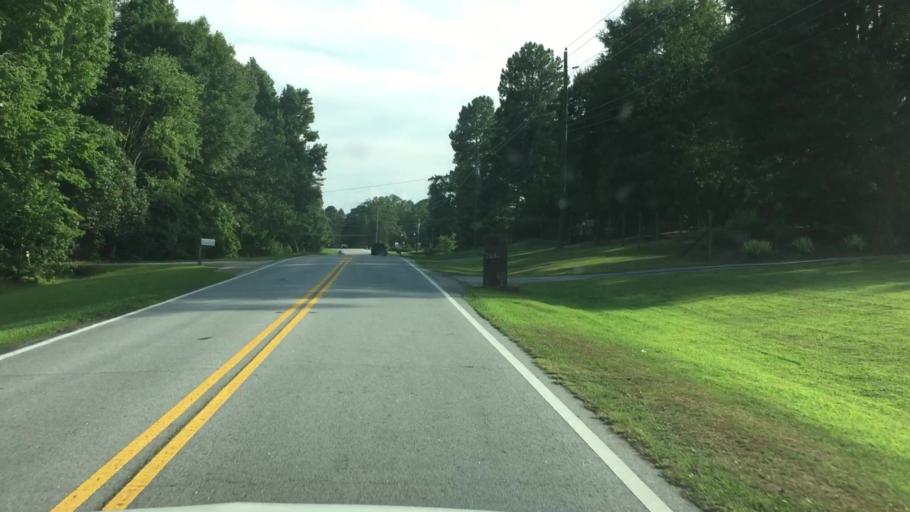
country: US
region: Georgia
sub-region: DeKalb County
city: Pine Mountain
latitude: 33.6158
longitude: -84.1349
